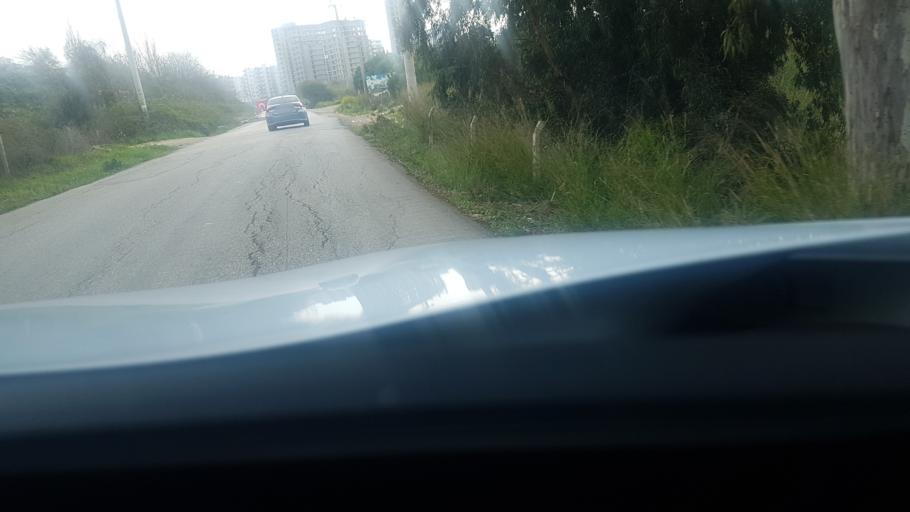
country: TR
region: Adana
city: Seyhan
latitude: 37.0561
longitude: 35.2538
